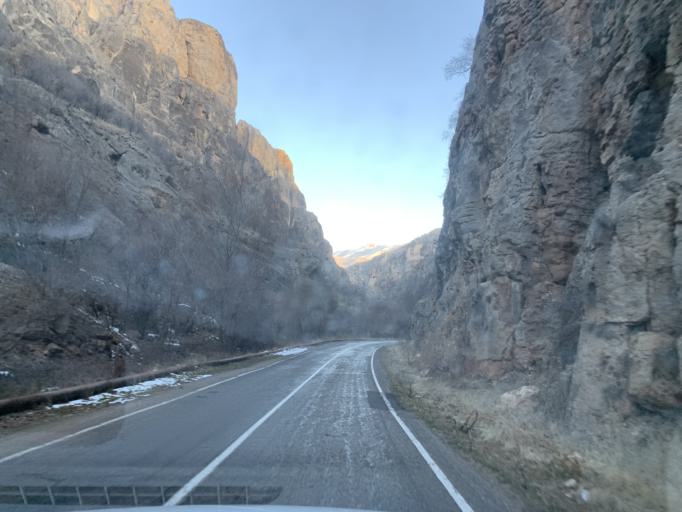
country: AM
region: Vayots' Dzori Marz
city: Areni
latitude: 39.7234
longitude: 45.2052
